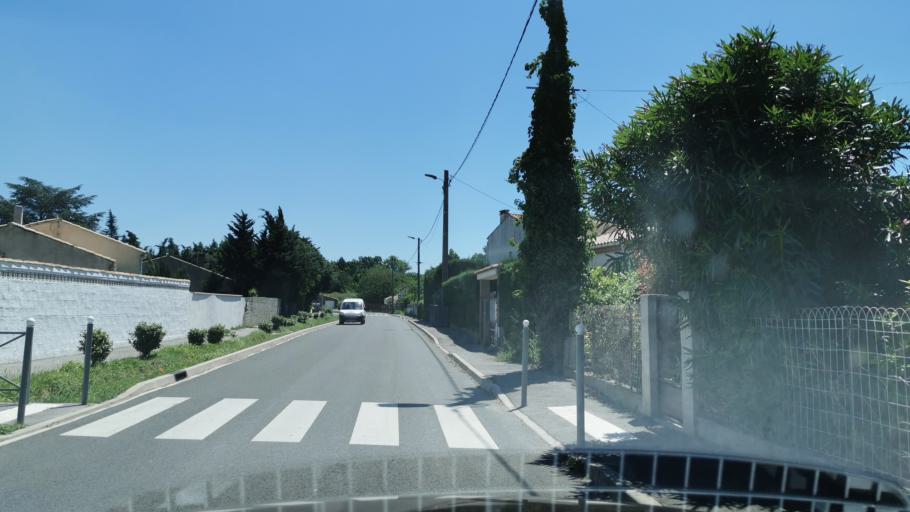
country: FR
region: Languedoc-Roussillon
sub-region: Departement de l'Aude
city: Moussan
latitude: 43.2454
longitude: 2.9873
